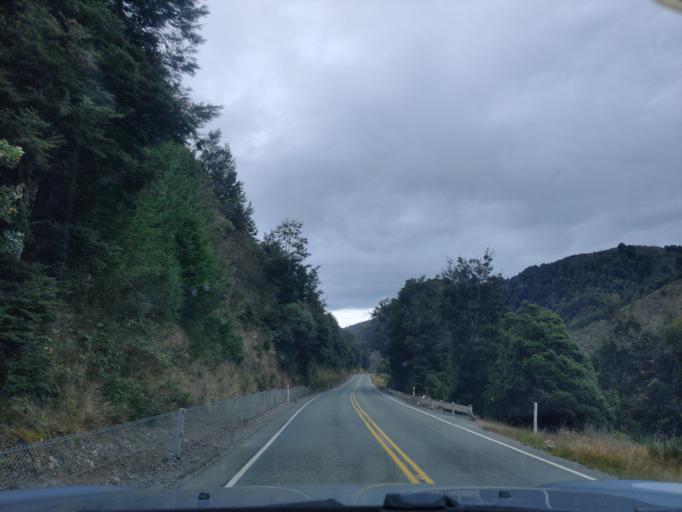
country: NZ
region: Tasman
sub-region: Tasman District
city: Wakefield
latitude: -41.7021
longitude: 172.6461
